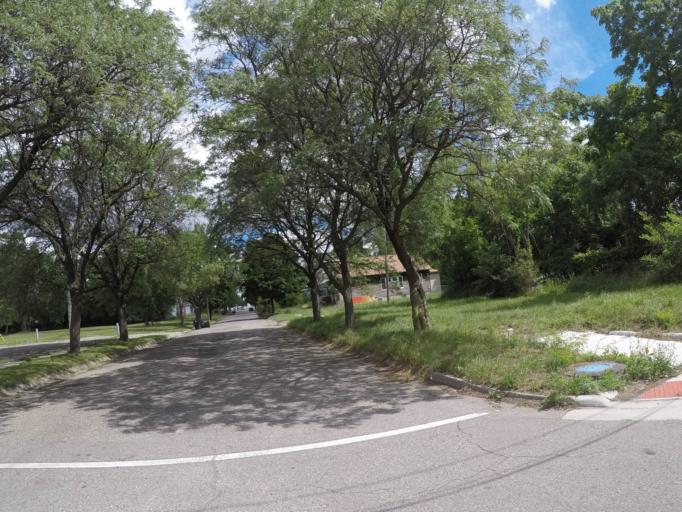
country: US
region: Michigan
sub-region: Wayne County
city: Hamtramck
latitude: 42.4189
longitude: -83.0581
